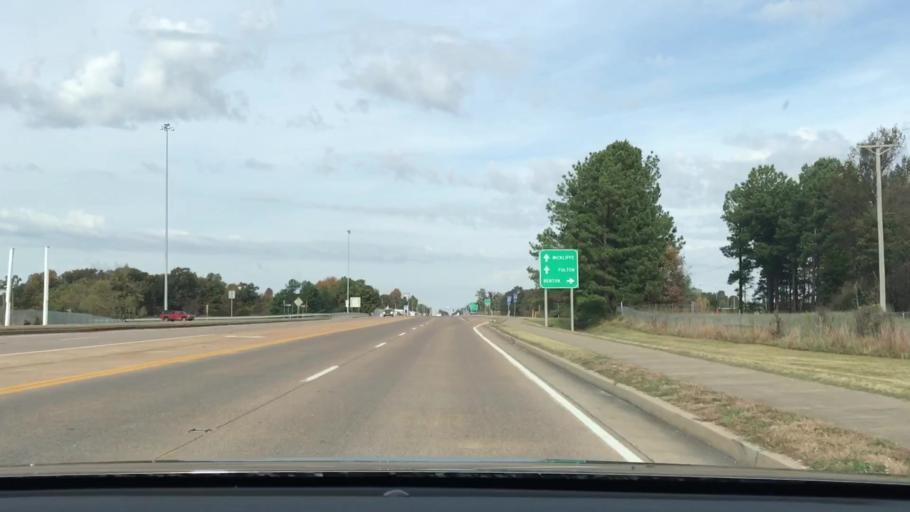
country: US
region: Kentucky
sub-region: Graves County
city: Mayfield
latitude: 36.7552
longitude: -88.6550
